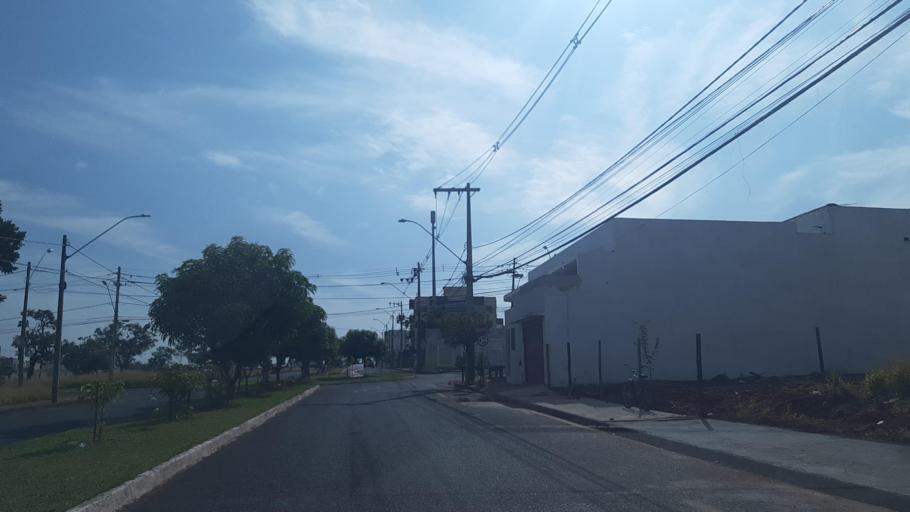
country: BR
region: Minas Gerais
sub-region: Uberlandia
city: Uberlandia
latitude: -18.8726
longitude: -48.2345
